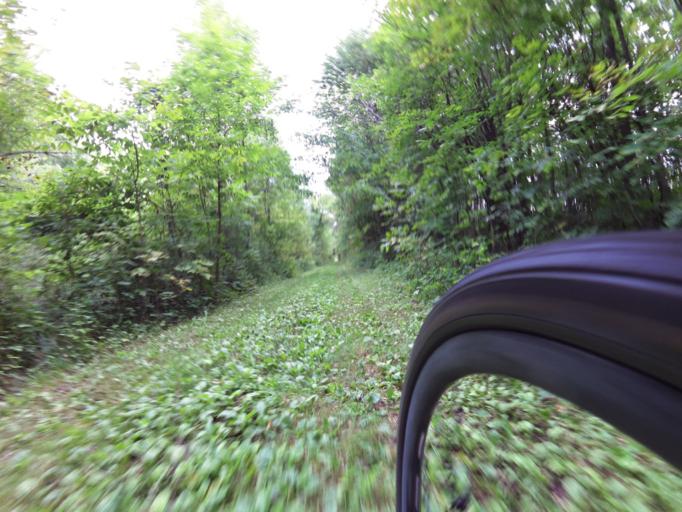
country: CA
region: Ontario
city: Perth
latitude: 44.6358
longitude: -76.2377
